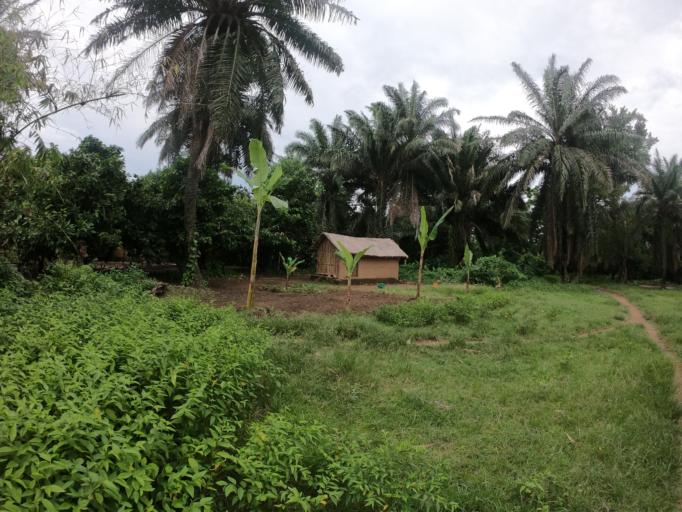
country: TZ
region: Mbeya
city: Kyela
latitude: -9.6591
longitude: 33.8372
